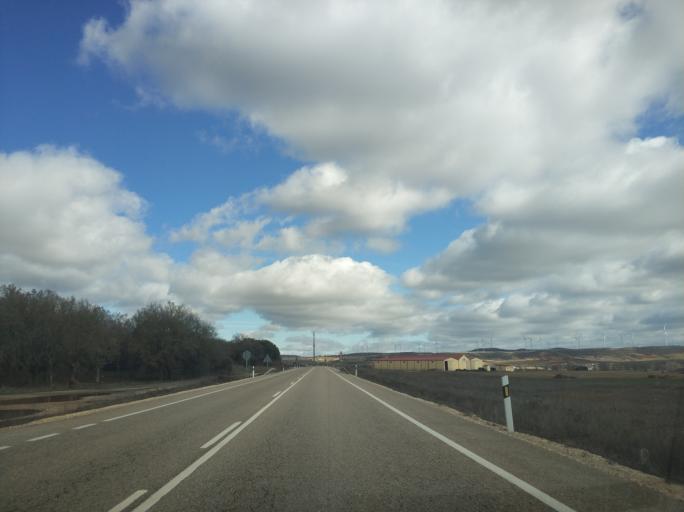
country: ES
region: Castille and Leon
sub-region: Provincia de Burgos
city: Revillarruz
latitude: 42.2167
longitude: -3.6529
